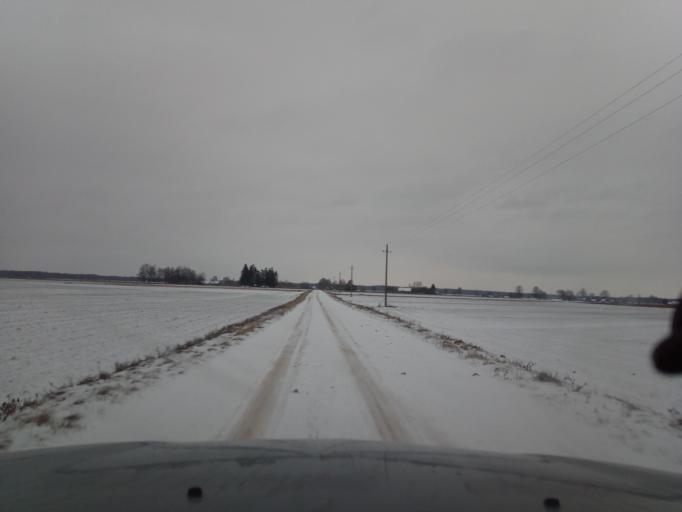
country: LT
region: Vilnius County
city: Ukmerge
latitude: 55.4815
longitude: 24.6086
